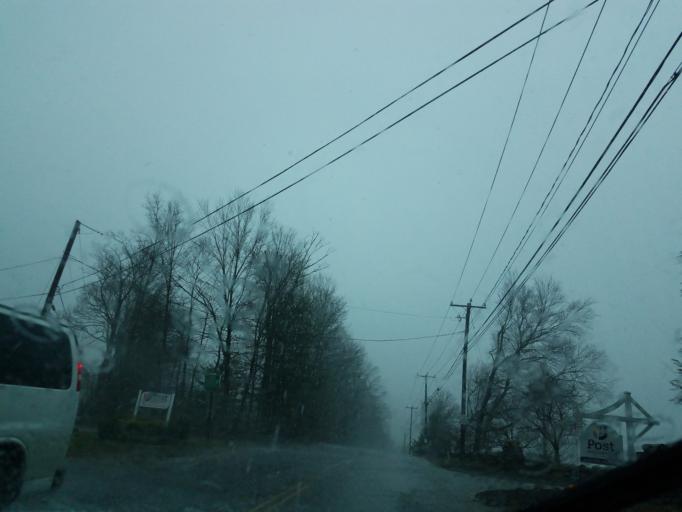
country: US
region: Connecticut
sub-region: New Haven County
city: Waterbury
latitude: 41.5348
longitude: -73.0803
